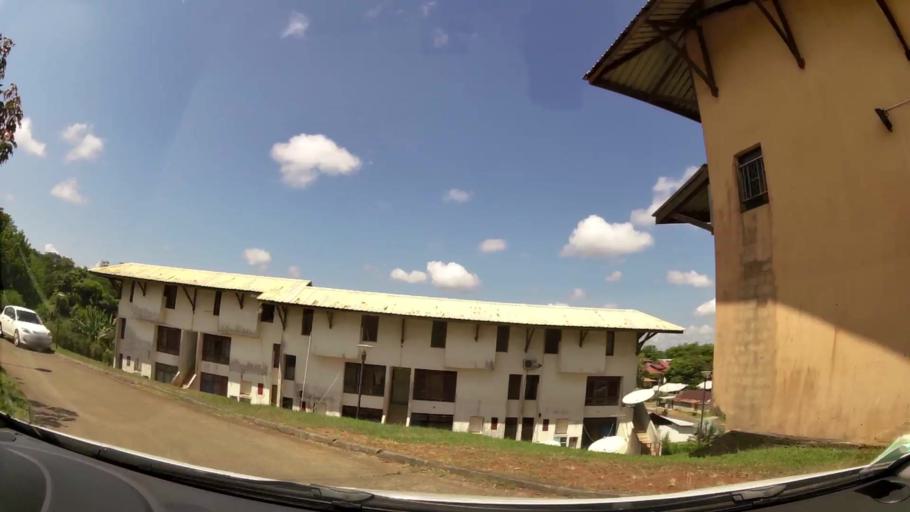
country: GF
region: Guyane
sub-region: Guyane
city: Cayenne
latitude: 4.9136
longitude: -52.3182
